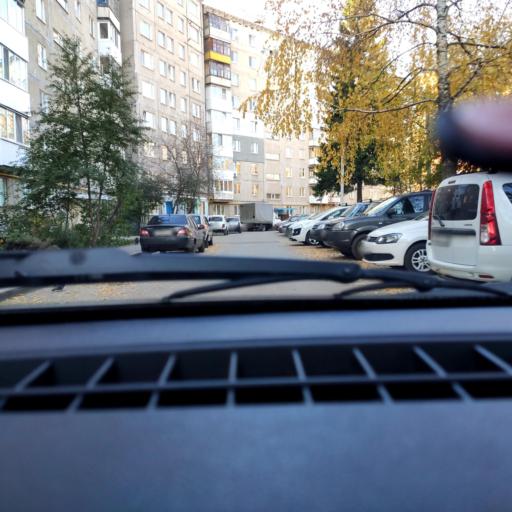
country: RU
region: Bashkortostan
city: Ufa
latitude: 54.7022
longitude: 55.9883
